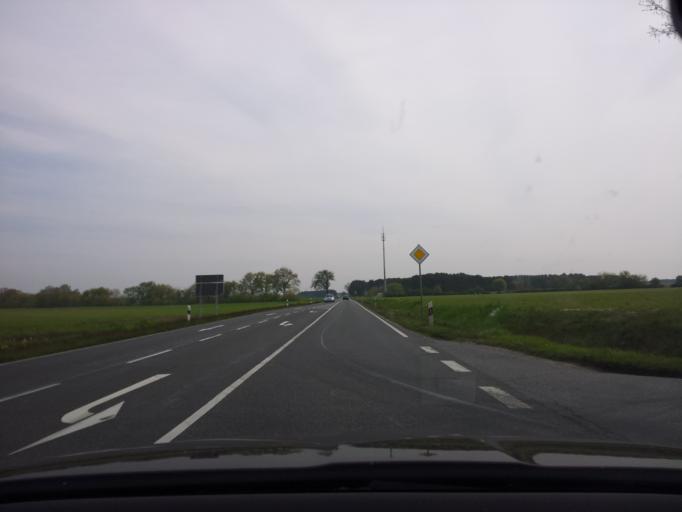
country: DE
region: Brandenburg
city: Luckau
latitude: 51.8858
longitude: 13.7833
